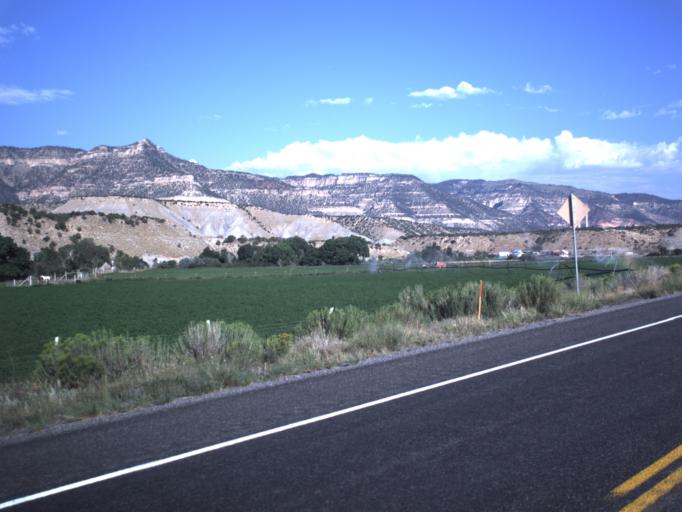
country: US
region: Utah
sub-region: Emery County
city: Huntington
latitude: 39.3590
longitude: -111.0309
